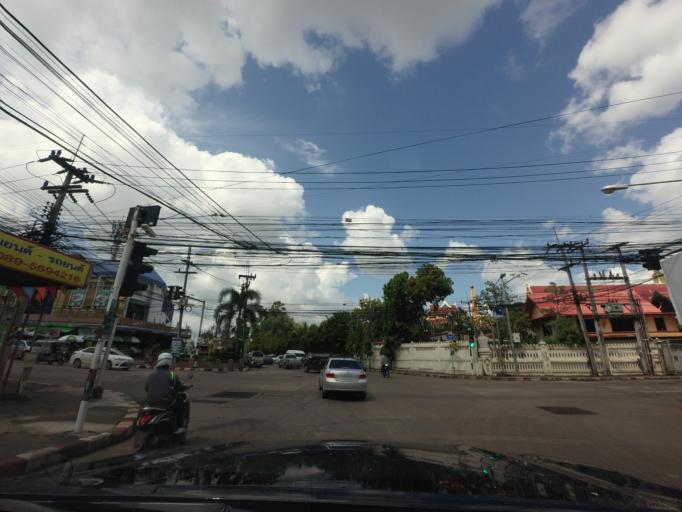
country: TH
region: Changwat Udon Thani
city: Udon Thani
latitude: 17.4132
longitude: 102.7771
